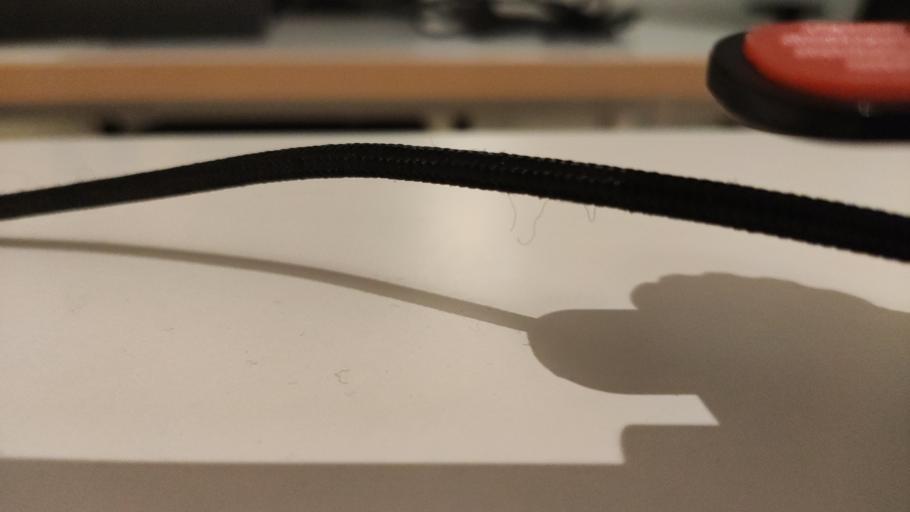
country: RU
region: Moskovskaya
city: Malaya Dubna
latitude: 55.8540
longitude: 38.9628
